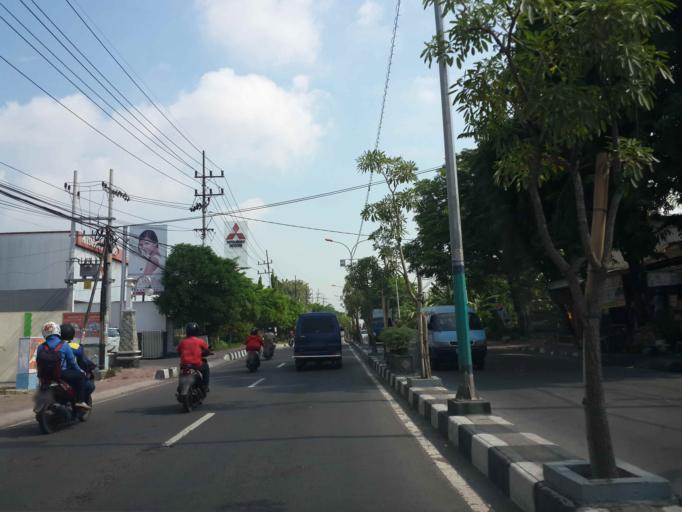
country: ID
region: East Java
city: Kebomas
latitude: -7.1837
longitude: 112.6486
